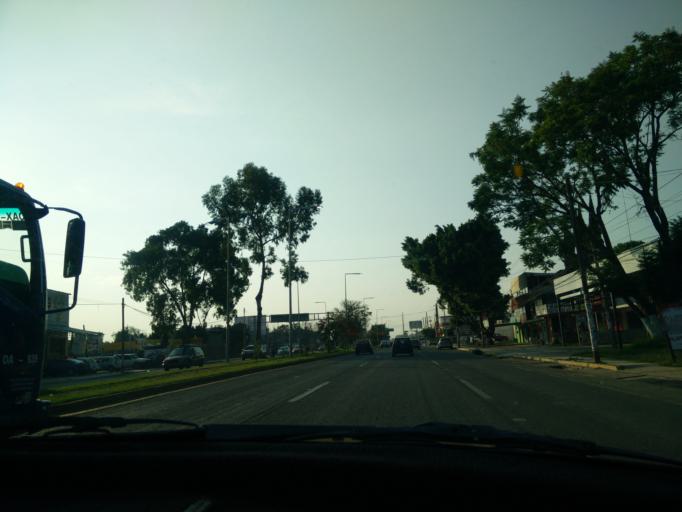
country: MX
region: Oaxaca
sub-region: Santa Maria Atzompa
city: San Jeronimo Yahuiche
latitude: 17.1205
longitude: -96.7626
